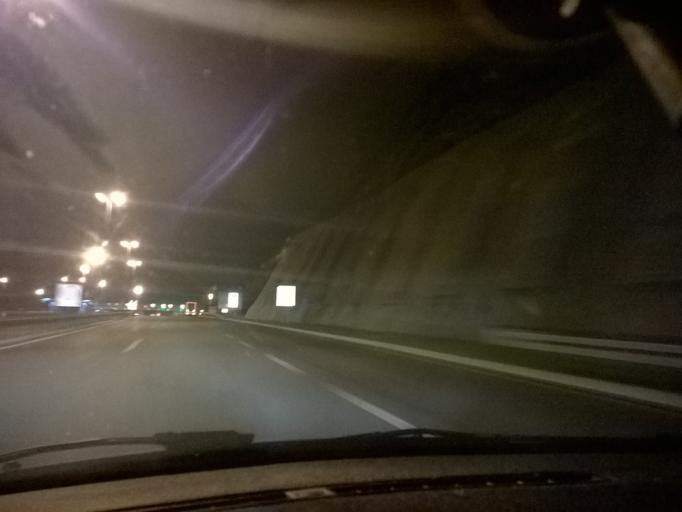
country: SI
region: Zetale
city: Zetale
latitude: 46.2696
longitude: 15.8676
